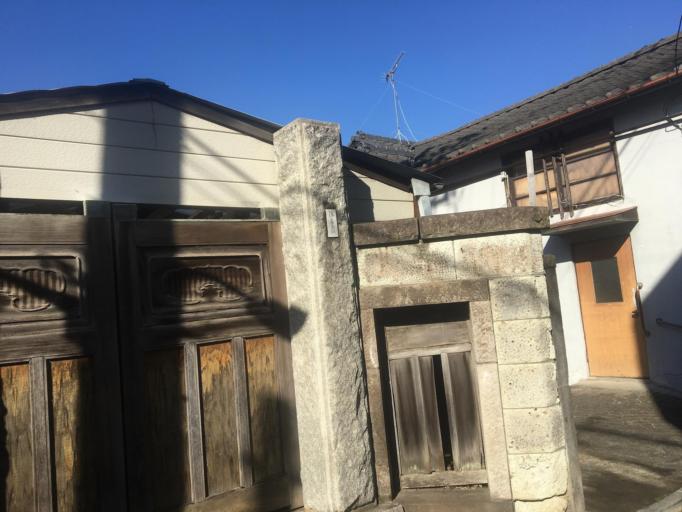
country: JP
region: Tokyo
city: Tokyo
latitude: 35.7356
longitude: 139.6980
